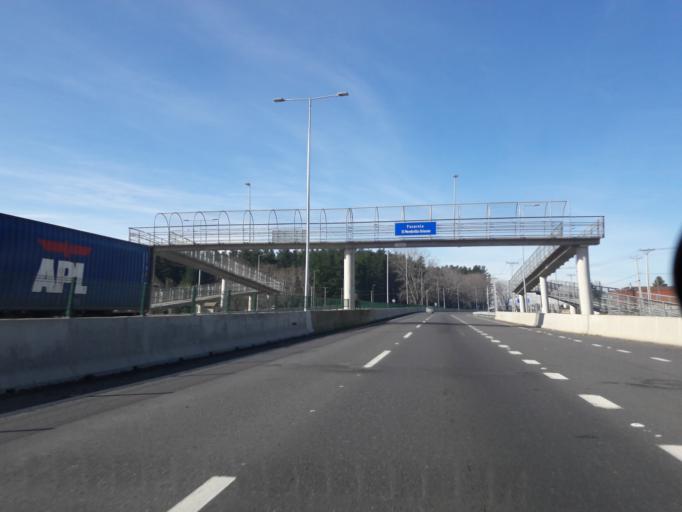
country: CL
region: Biobio
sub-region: Provincia de Biobio
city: Cabrero
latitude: -37.0318
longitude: -72.4235
